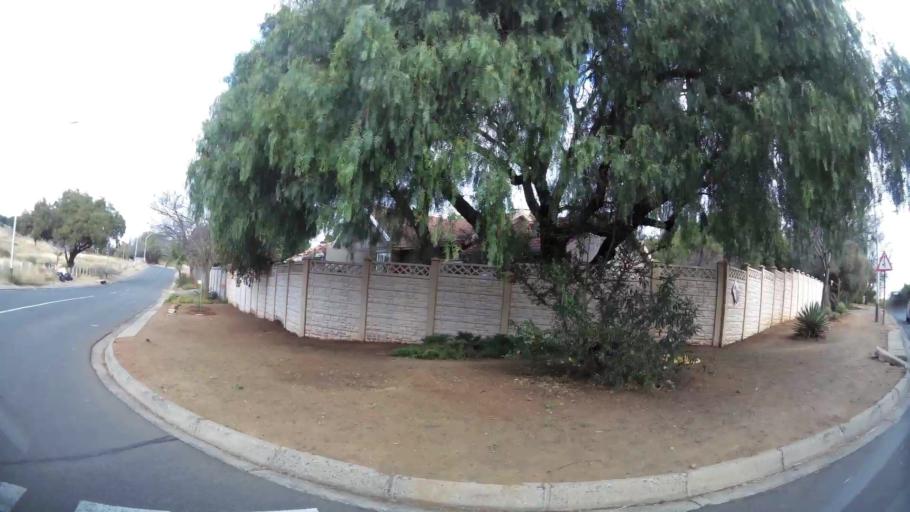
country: ZA
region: Orange Free State
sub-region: Mangaung Metropolitan Municipality
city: Bloemfontein
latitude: -29.0762
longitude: 26.2070
